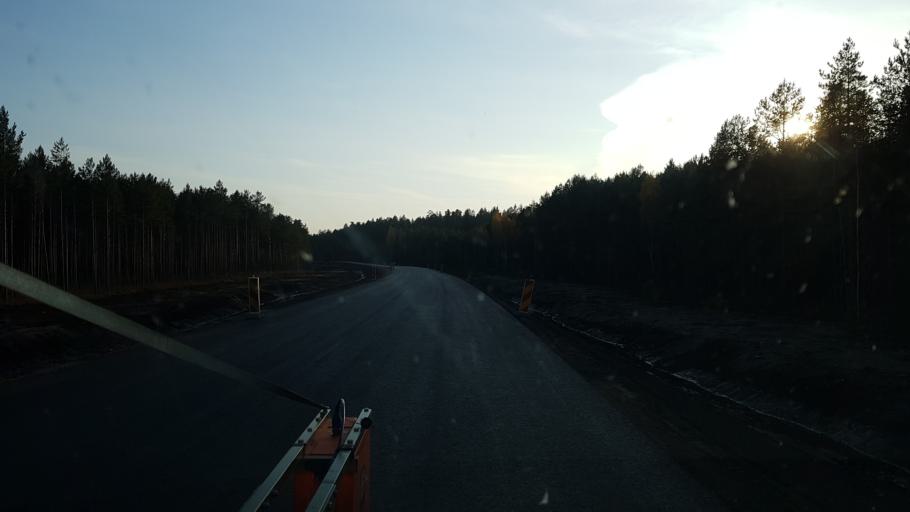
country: EE
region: Polvamaa
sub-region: Polva linn
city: Polva
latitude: 57.9330
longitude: 27.1862
